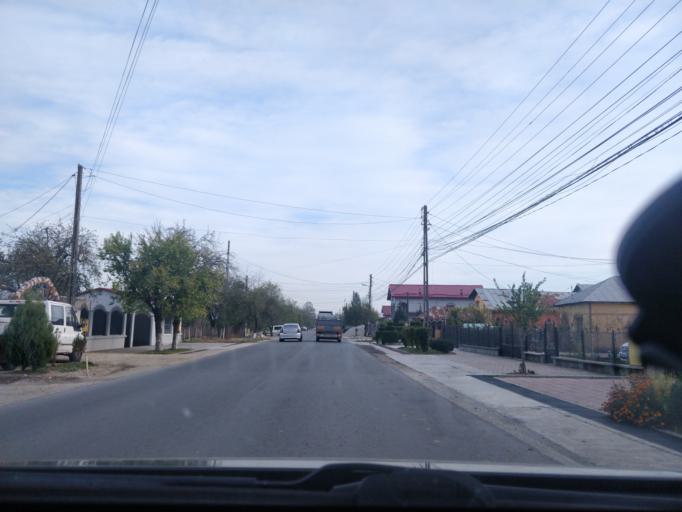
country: RO
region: Giurgiu
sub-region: Comuna Bolintin Vale
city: Malu Spart
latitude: 44.4381
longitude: 25.7198
